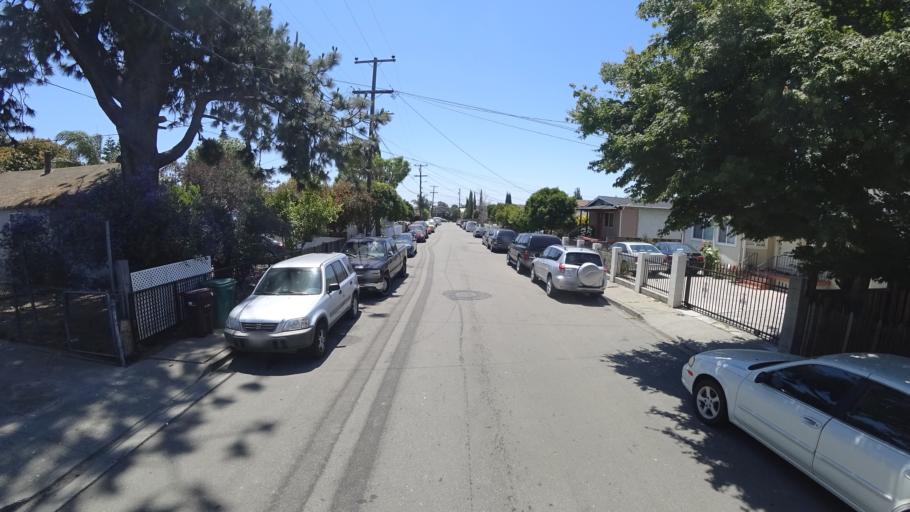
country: US
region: California
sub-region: Alameda County
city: Hayward
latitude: 37.6621
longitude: -122.0831
